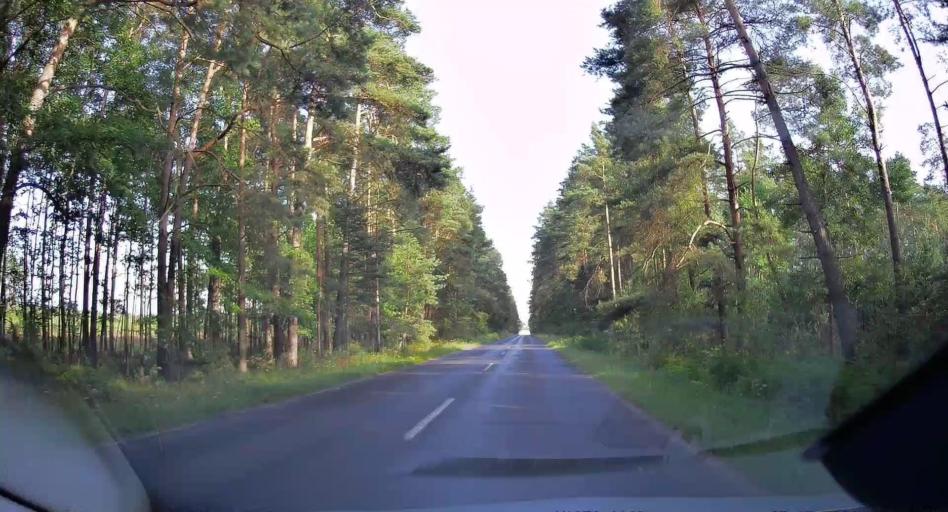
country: PL
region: Swietokrzyskie
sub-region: Powiat konecki
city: Smykow
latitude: 51.0908
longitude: 20.3668
